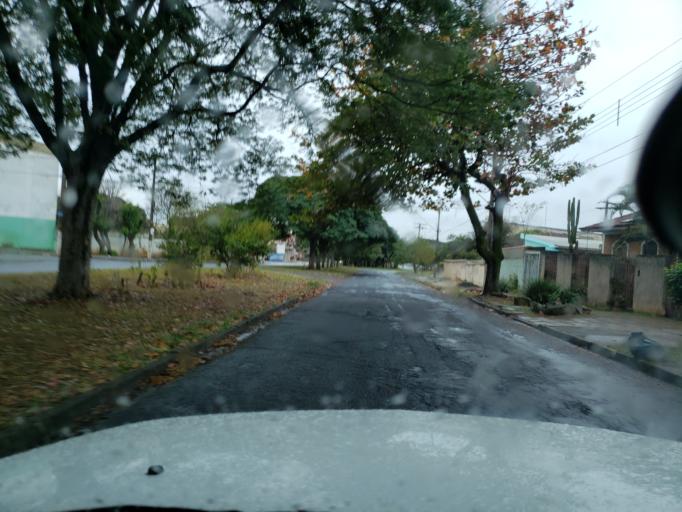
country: BR
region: Sao Paulo
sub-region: Moji-Guacu
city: Mogi-Gaucu
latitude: -22.3510
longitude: -46.9416
